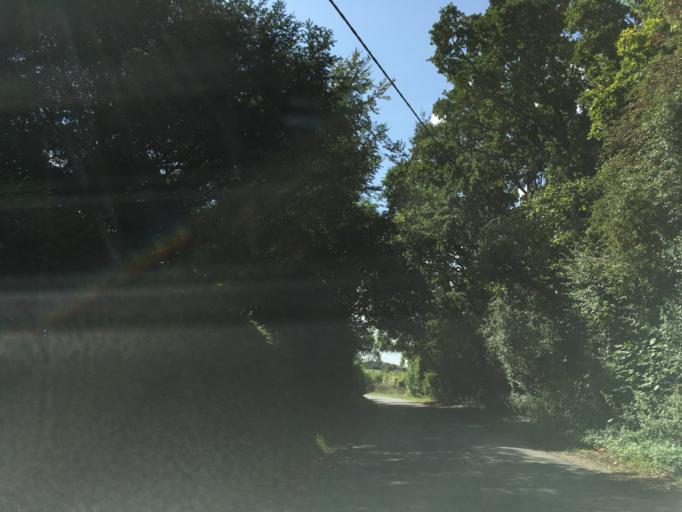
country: GB
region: England
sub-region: Hampshire
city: Colden Common
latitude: 51.0071
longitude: -1.2854
